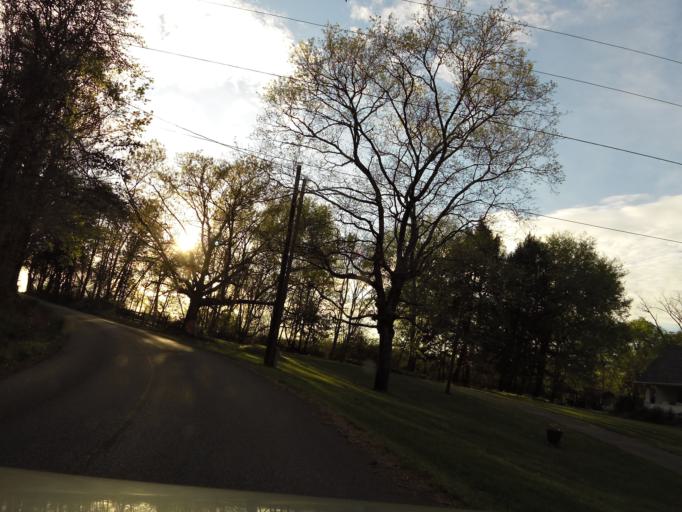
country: US
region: Tennessee
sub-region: Loudon County
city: Greenback
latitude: 35.6362
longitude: -84.0563
